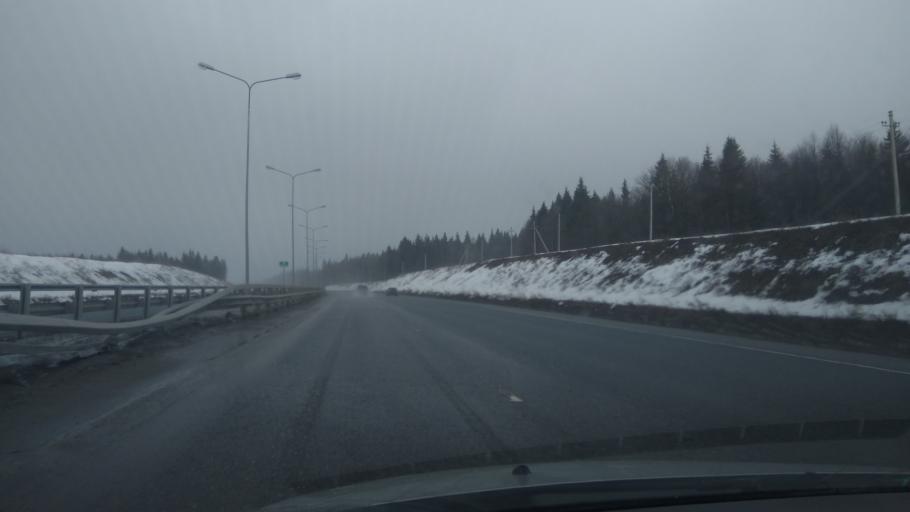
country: RU
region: Perm
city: Zvezdnyy
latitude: 57.7666
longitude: 56.3341
